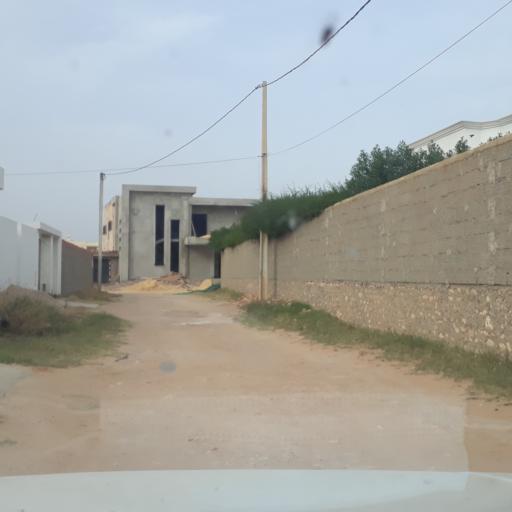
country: TN
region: Safaqis
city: Al Qarmadah
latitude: 34.8205
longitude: 10.7758
